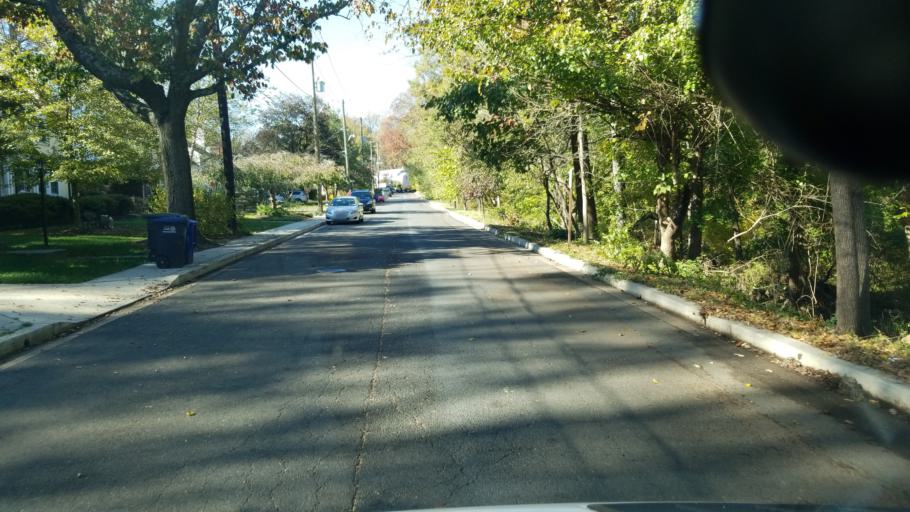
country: US
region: Maryland
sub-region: Montgomery County
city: Chevy Chase
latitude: 38.9778
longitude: -77.0613
